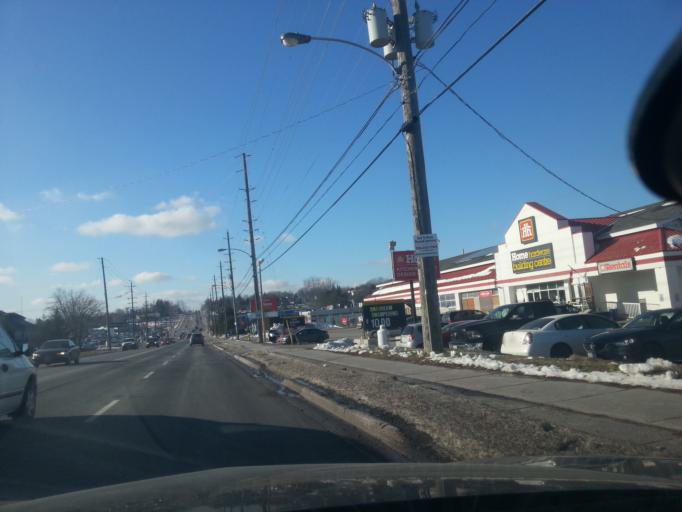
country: CA
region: Ontario
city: Peterborough
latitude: 44.2785
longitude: -78.3598
